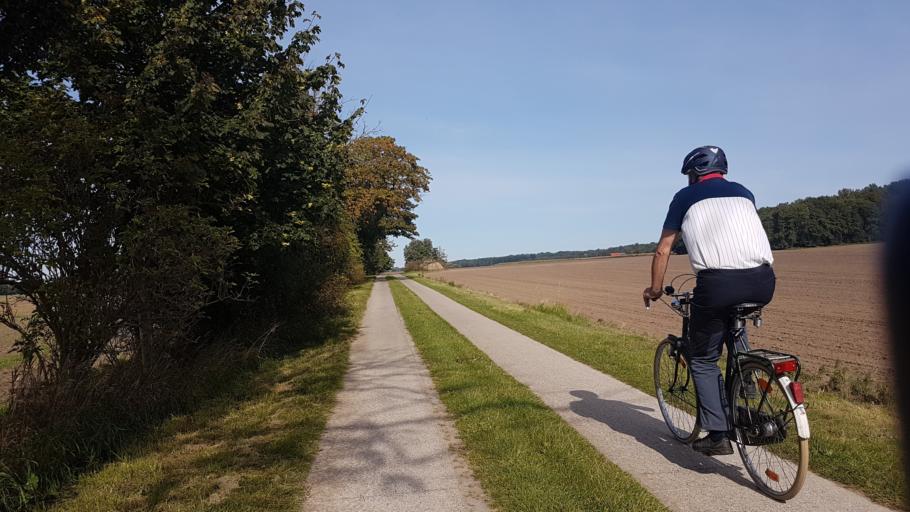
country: DE
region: Mecklenburg-Vorpommern
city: Gingst
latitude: 54.4109
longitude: 13.2573
